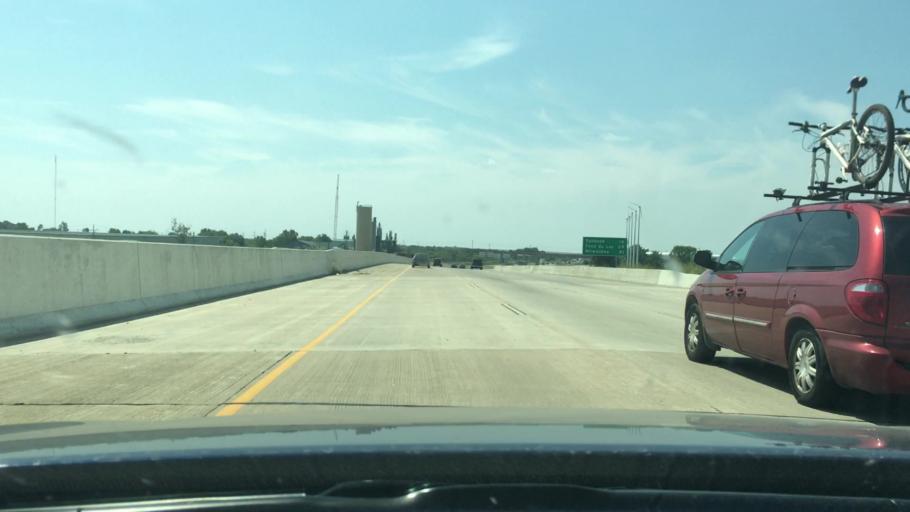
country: US
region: Wisconsin
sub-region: Winnebago County
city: Neenah
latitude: 44.1499
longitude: -88.4872
